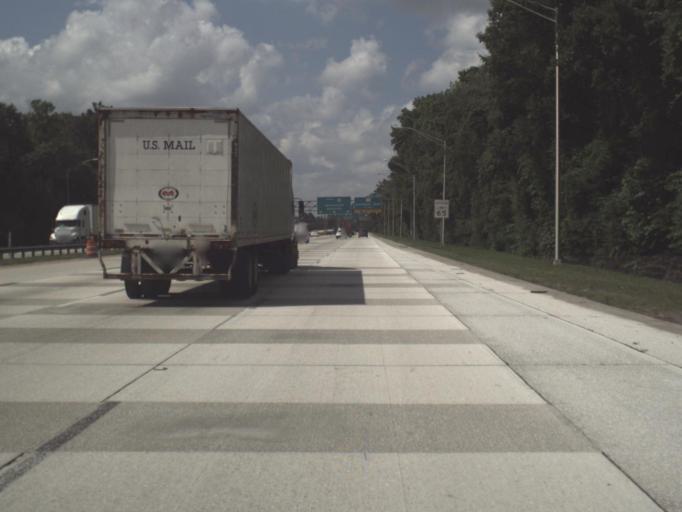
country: US
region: Florida
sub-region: Saint Johns County
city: Fruit Cove
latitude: 30.1899
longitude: -81.5570
